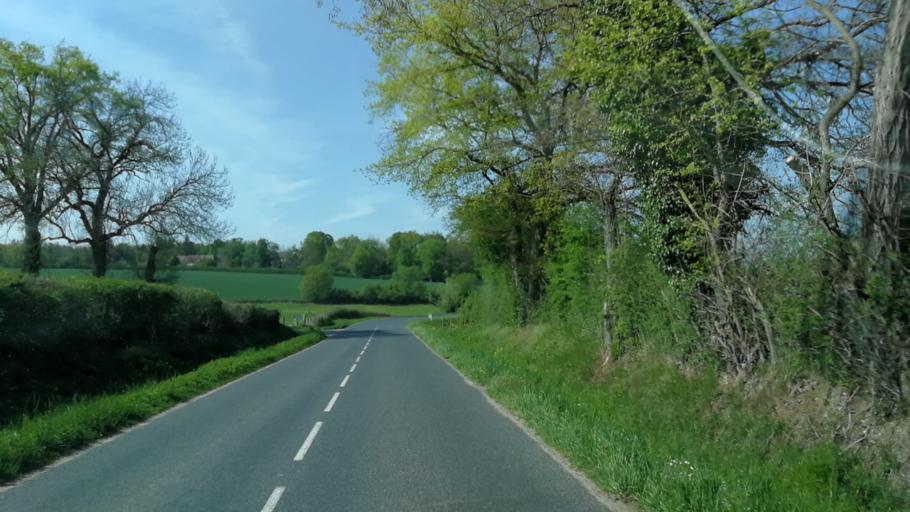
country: FR
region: Auvergne
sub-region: Departement de l'Allier
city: Saint-Gerand-le-Puy
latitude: 46.3421
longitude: 3.5792
